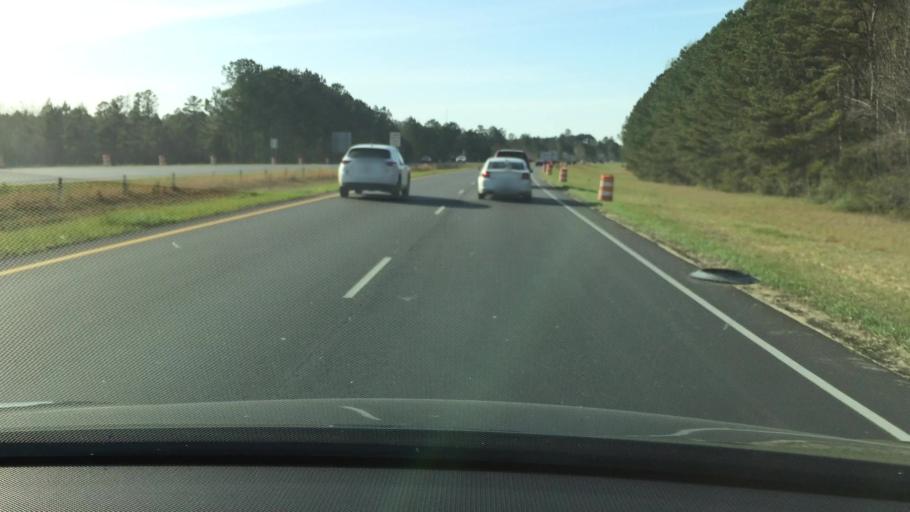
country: US
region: North Carolina
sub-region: Johnston County
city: Pine Level
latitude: 35.4939
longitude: -78.2743
